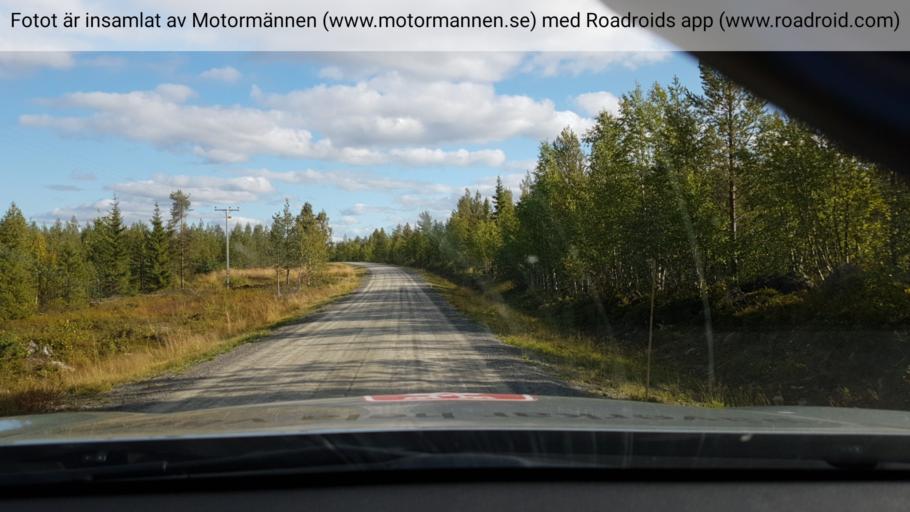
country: SE
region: Vaesterbotten
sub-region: Sorsele Kommun
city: Sorsele
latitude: 65.4605
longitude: 17.6978
